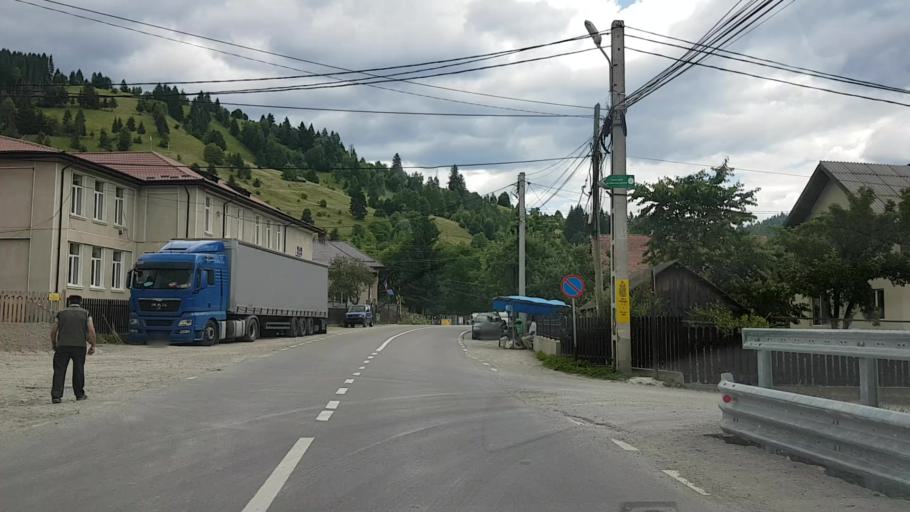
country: RO
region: Neamt
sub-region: Comuna Farcasa
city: Farcasa
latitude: 47.1564
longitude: 25.8384
